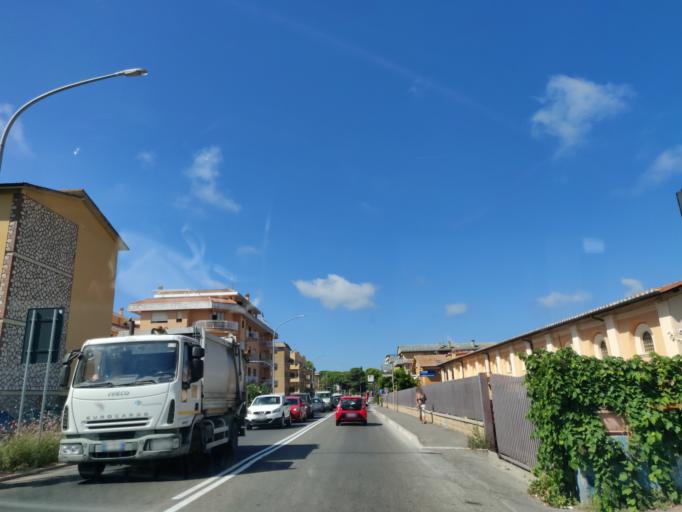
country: IT
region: Tuscany
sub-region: Provincia di Grosseto
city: Orbetello
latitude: 42.4422
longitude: 11.2203
